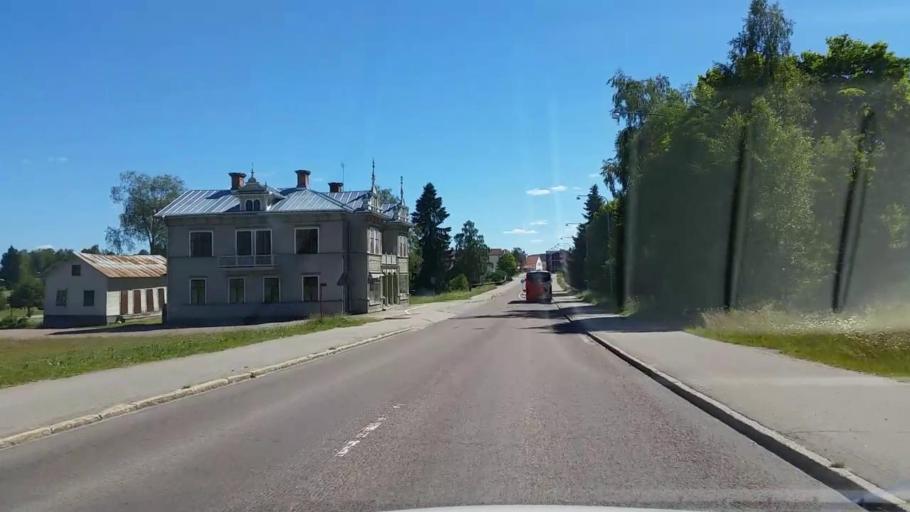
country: SE
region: Gaevleborg
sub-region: Ovanakers Kommun
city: Edsbyn
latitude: 61.3836
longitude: 15.8127
